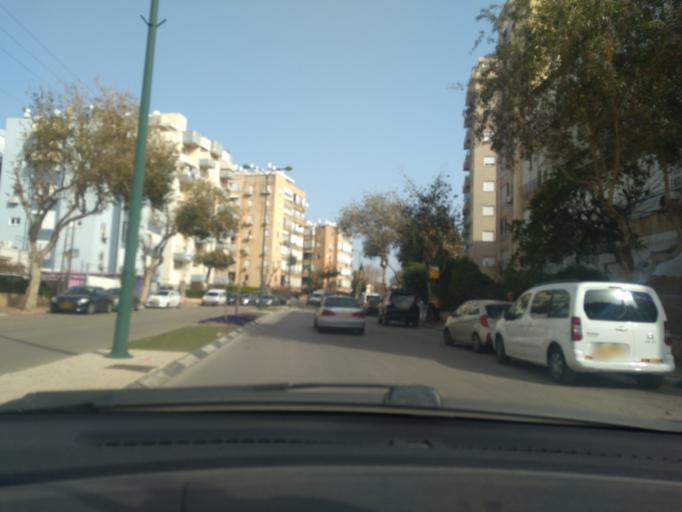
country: IL
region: Central District
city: Netanya
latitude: 32.3316
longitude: 34.8614
